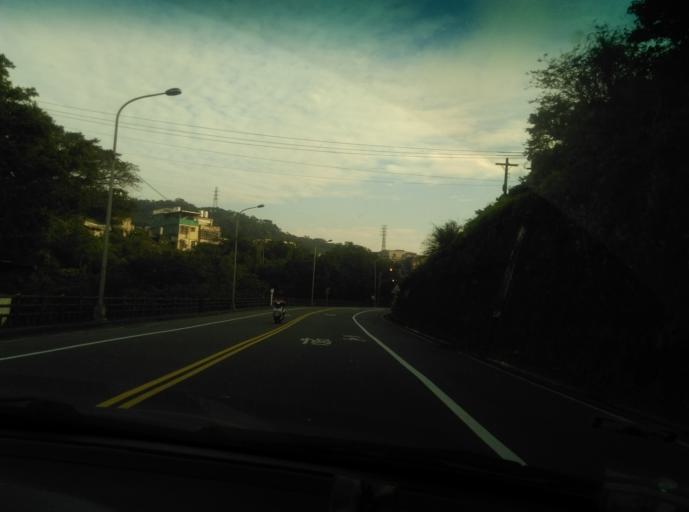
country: TW
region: Taiwan
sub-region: Keelung
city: Keelung
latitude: 25.1504
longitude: 121.7364
